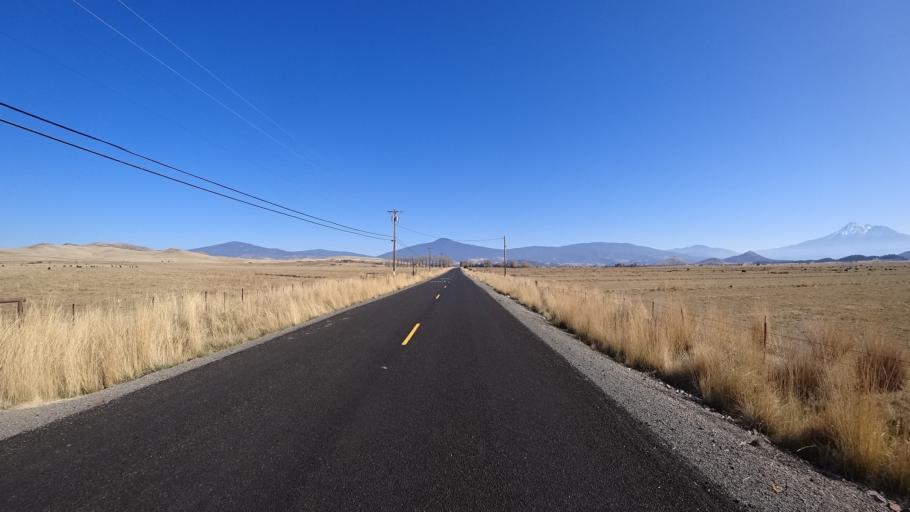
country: US
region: California
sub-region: Siskiyou County
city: Montague
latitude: 41.7244
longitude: -122.4552
